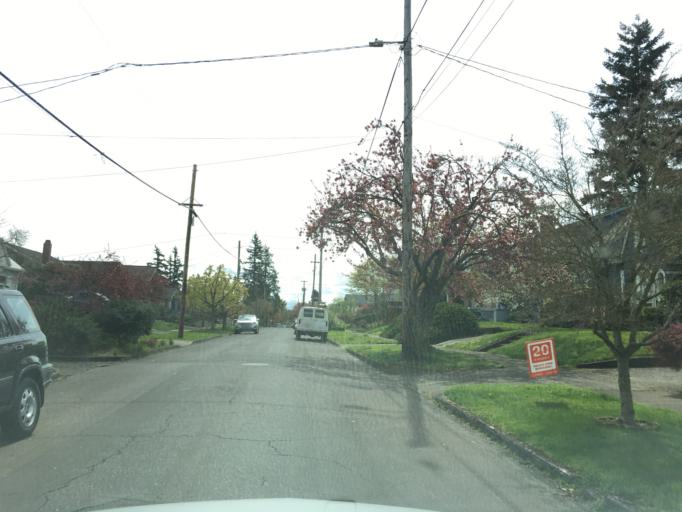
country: US
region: Oregon
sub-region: Multnomah County
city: Lents
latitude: 45.5463
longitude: -122.5984
